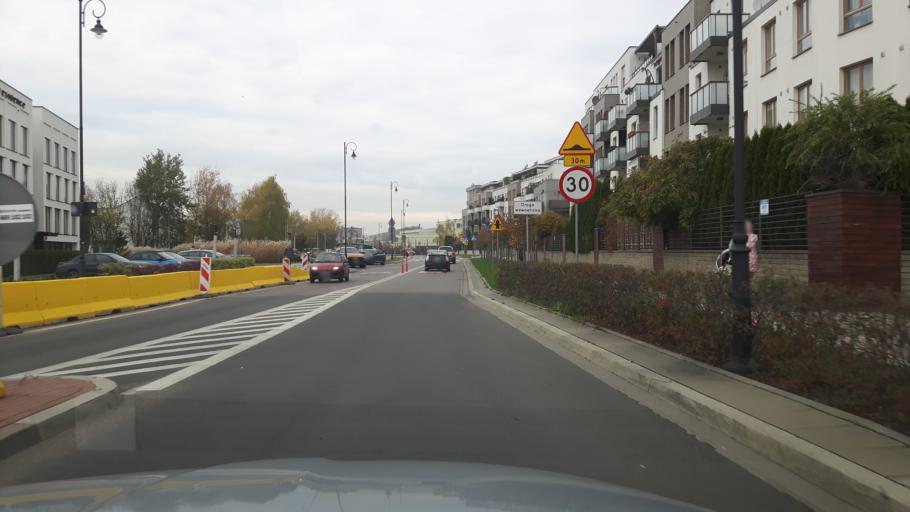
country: PL
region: Masovian Voivodeship
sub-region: Warszawa
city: Wilanow
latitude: 52.1549
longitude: 21.0708
